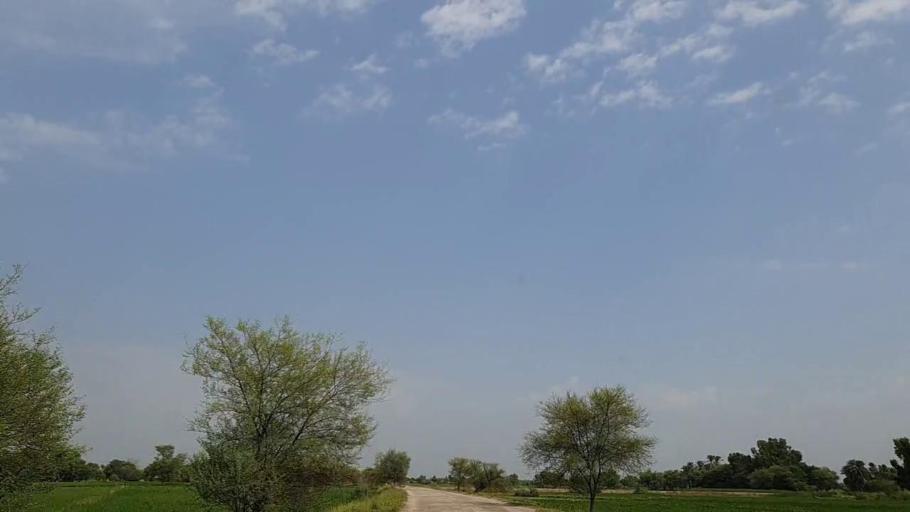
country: PK
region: Sindh
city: Khanpur
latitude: 27.8398
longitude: 69.4678
